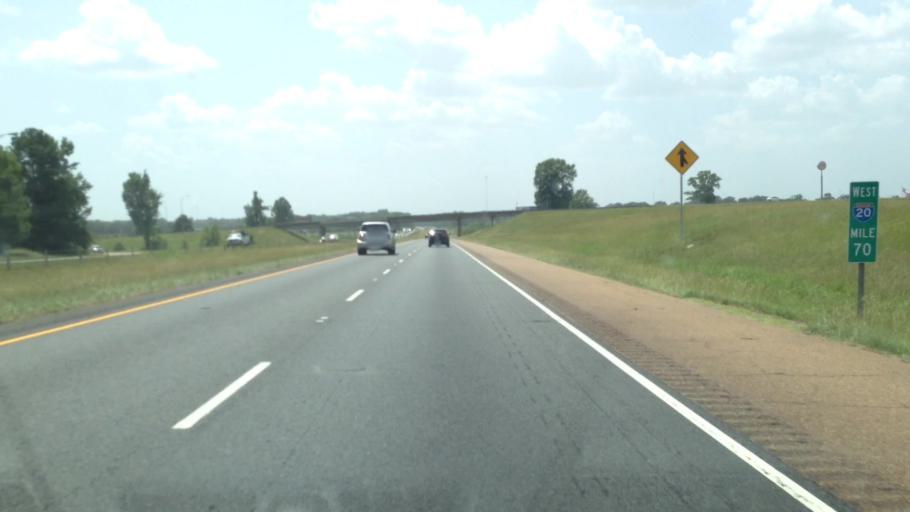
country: US
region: Louisiana
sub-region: Bienville Parish
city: Arcadia
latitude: 32.5629
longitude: -92.9070
